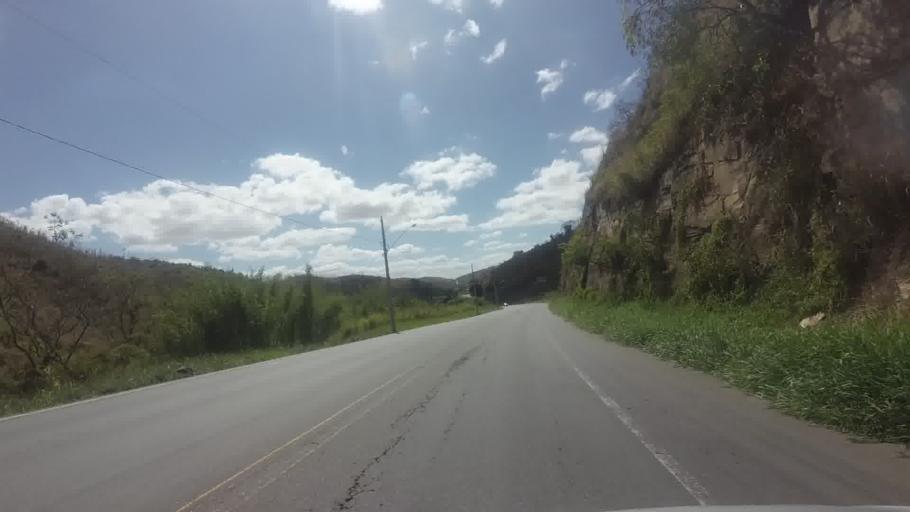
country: BR
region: Minas Gerais
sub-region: Alem Paraiba
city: Alem Paraiba
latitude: -21.8610
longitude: -42.6667
